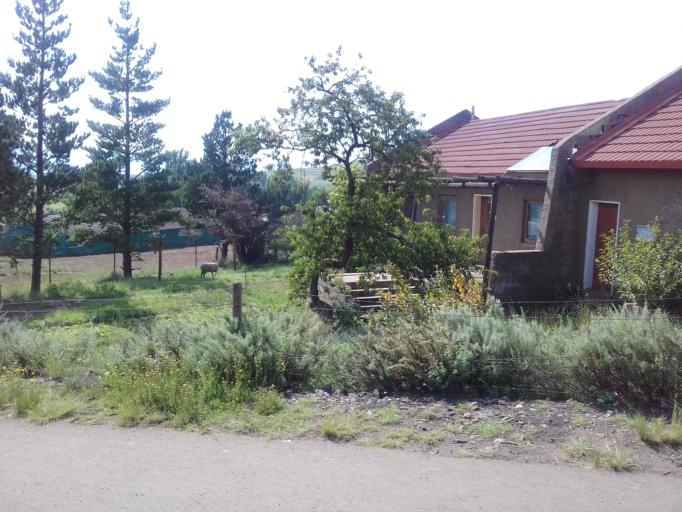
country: LS
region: Thaba-Tseka
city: Thaba-Tseka
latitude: -29.5231
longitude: 28.6085
